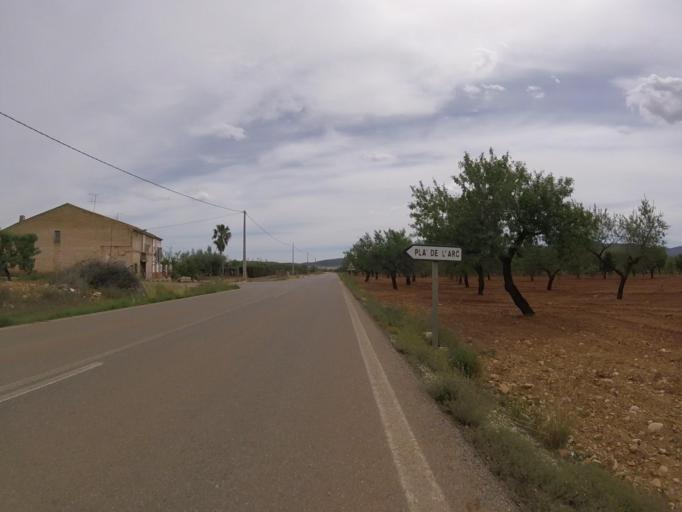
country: ES
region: Valencia
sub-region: Provincia de Castello
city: Cabanes
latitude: 40.1675
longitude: 0.0044
